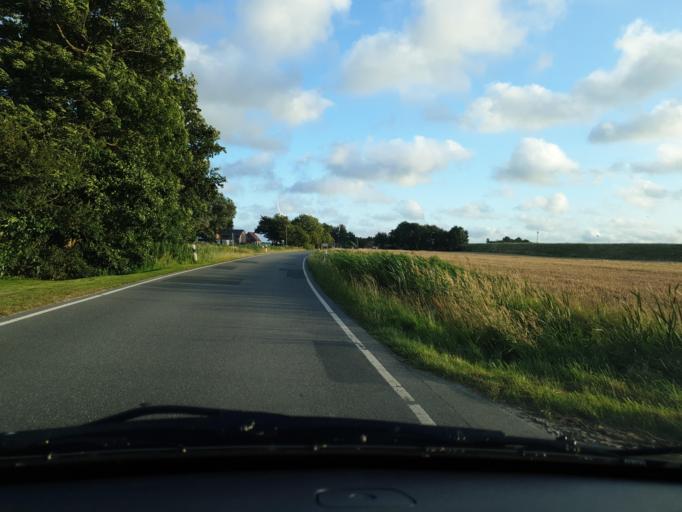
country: DE
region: Schleswig-Holstein
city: Busenwurth
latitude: 54.0294
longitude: 9.0193
